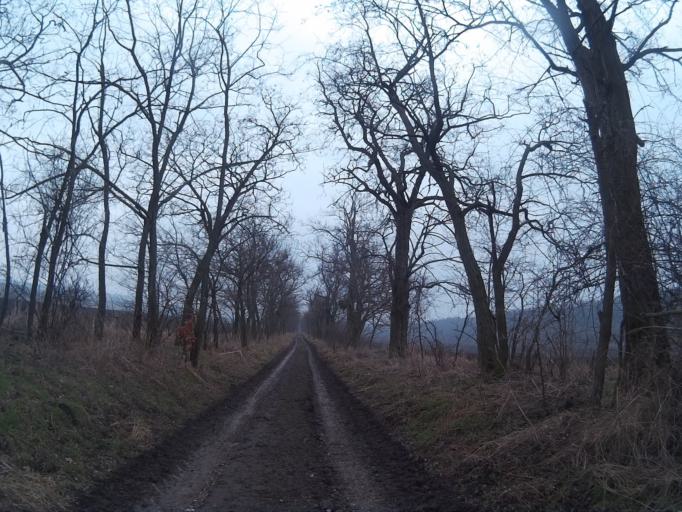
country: HU
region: Komarom-Esztergom
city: Tarjan
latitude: 47.5561
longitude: 18.5575
